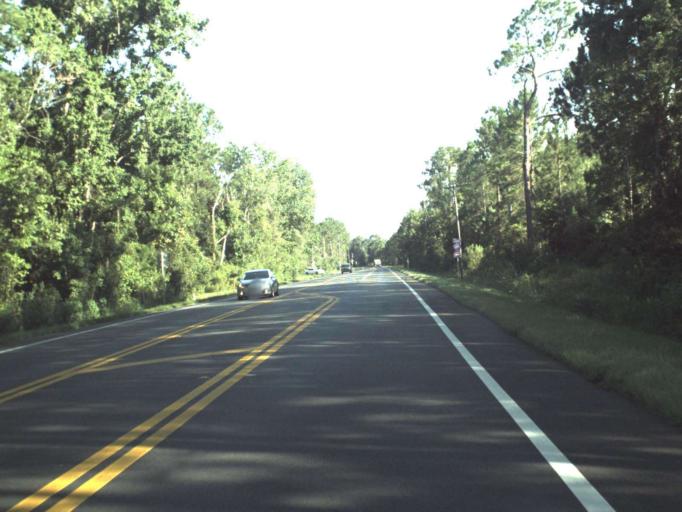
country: US
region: Florida
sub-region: Lake County
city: Clermont
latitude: 28.3782
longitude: -81.8236
